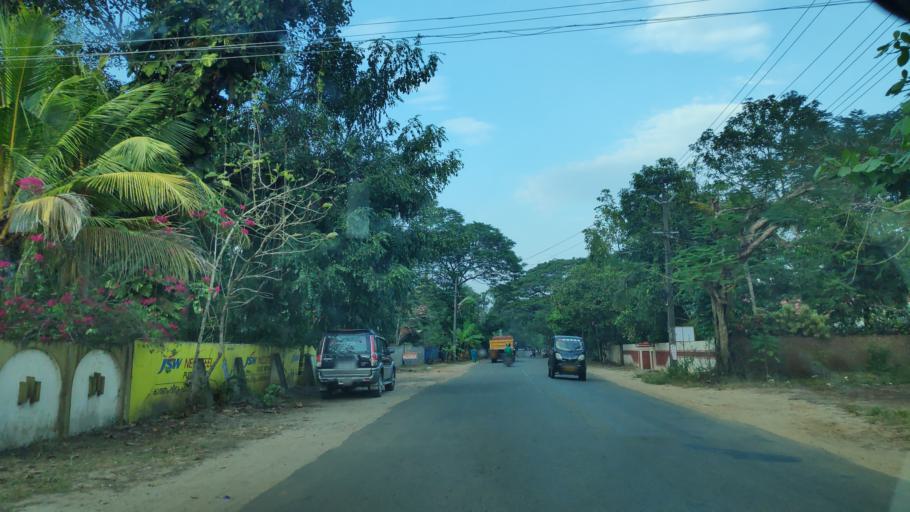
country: IN
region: Kerala
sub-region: Alappuzha
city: Shertallai
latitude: 9.6534
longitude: 76.3745
